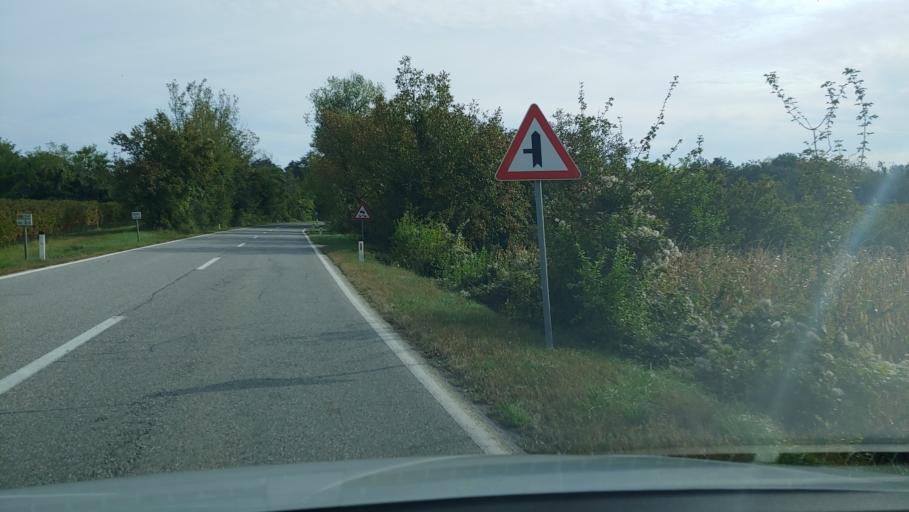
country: SI
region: Nova Gorica
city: Sempas
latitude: 45.9144
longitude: 13.7671
